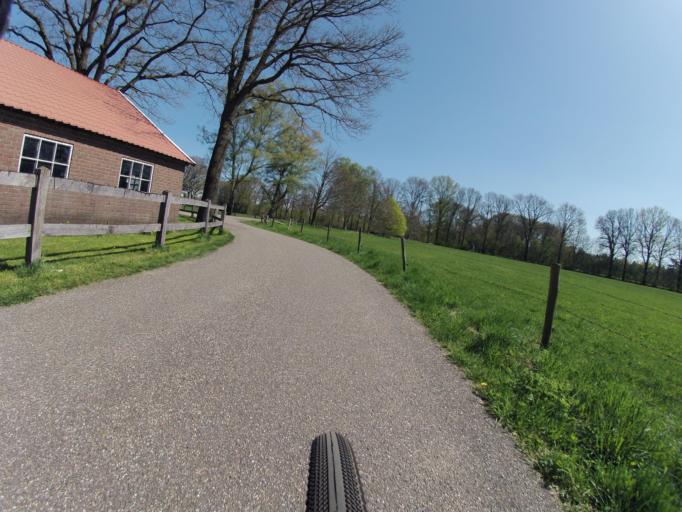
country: NL
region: Overijssel
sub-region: Gemeente Losser
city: Losser
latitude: 52.2713
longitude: 6.9693
